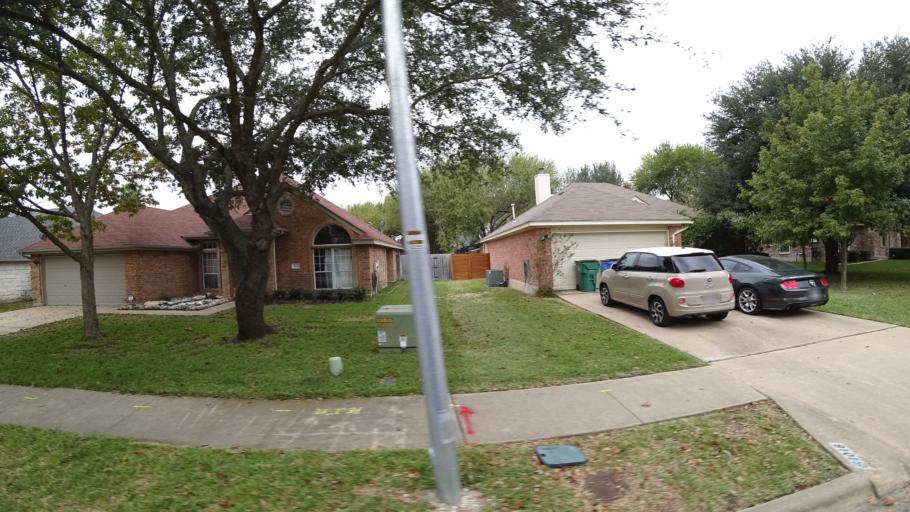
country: US
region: Texas
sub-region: Travis County
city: Pflugerville
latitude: 30.4456
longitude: -97.6096
